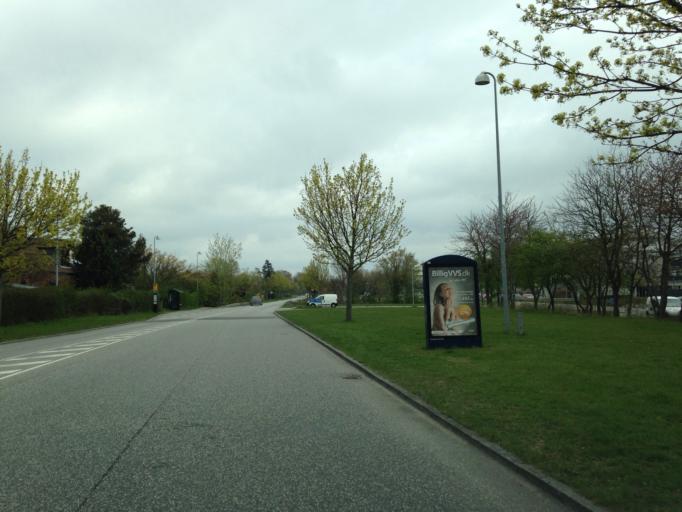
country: DK
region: Capital Region
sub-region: Ishoj Kommune
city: Ishoj
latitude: 55.6017
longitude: 12.3247
